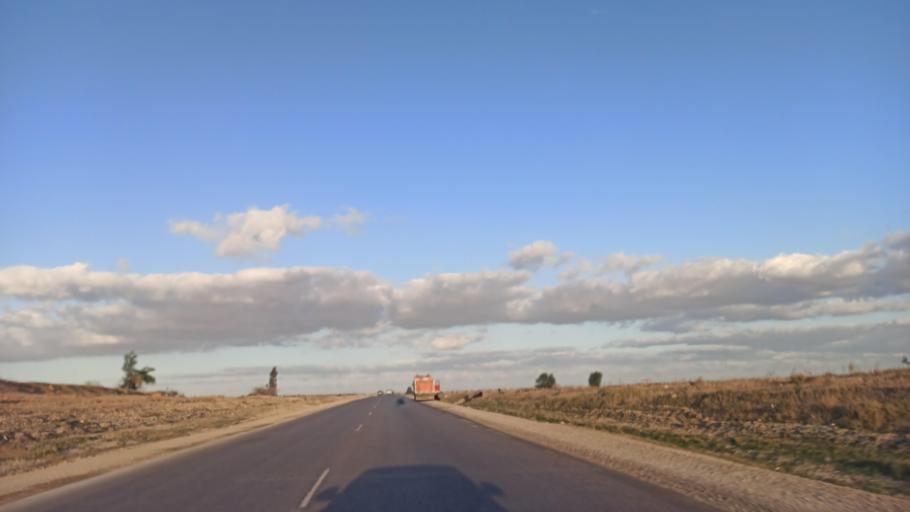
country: TN
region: Al Qayrawan
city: Sbikha
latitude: 35.8876
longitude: 10.2408
